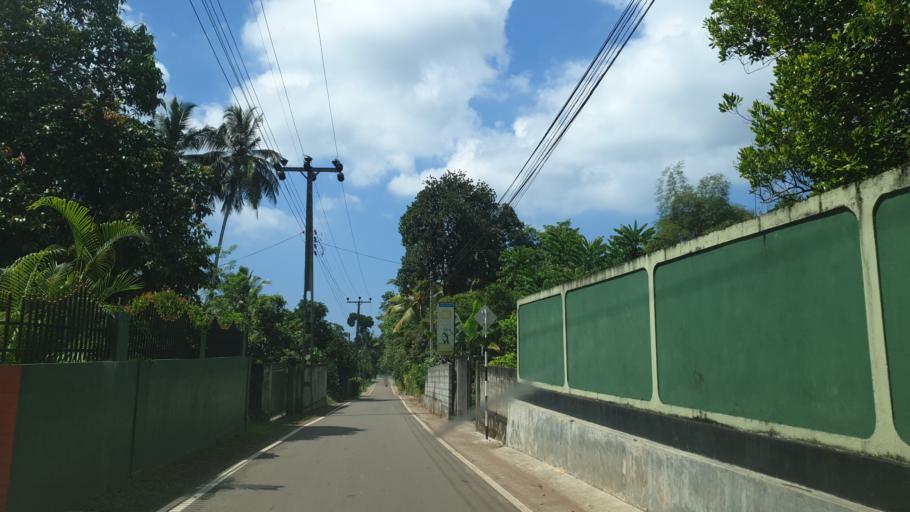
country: LK
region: Western
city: Panadura
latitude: 6.6757
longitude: 79.9683
